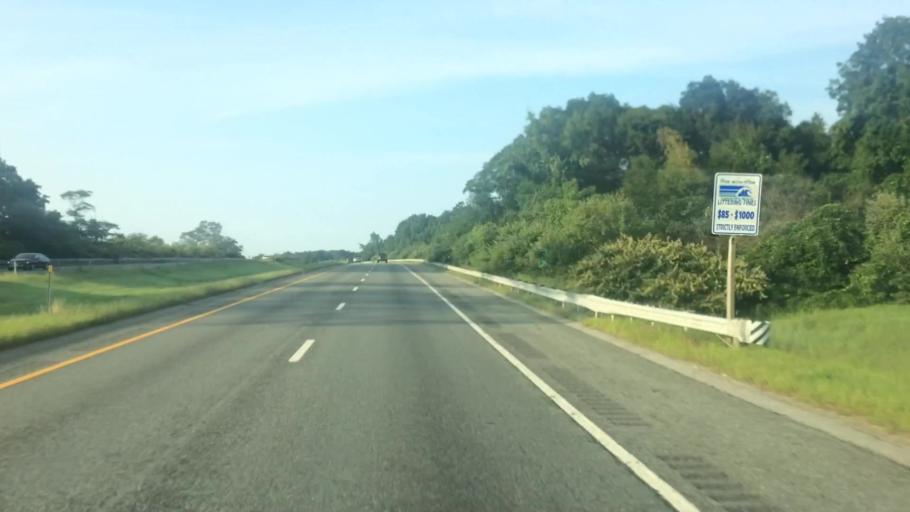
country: US
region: Rhode Island
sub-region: Washington County
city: Exeter
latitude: 41.6052
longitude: -71.4976
